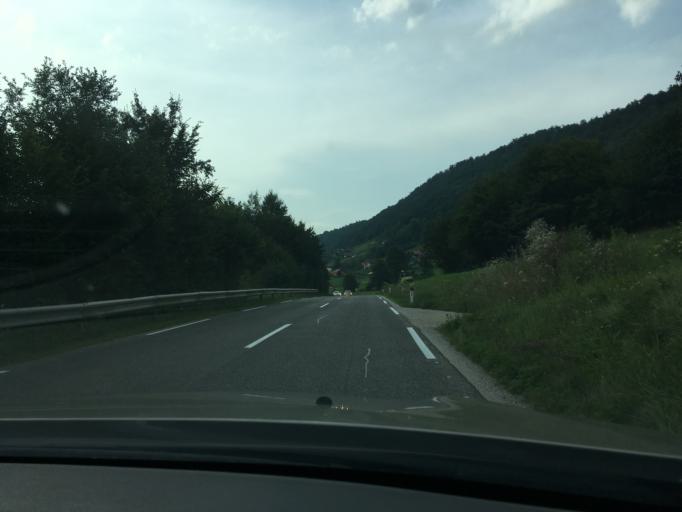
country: SI
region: Zuzemberk
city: Zuzemberk
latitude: 45.7933
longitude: 14.9874
